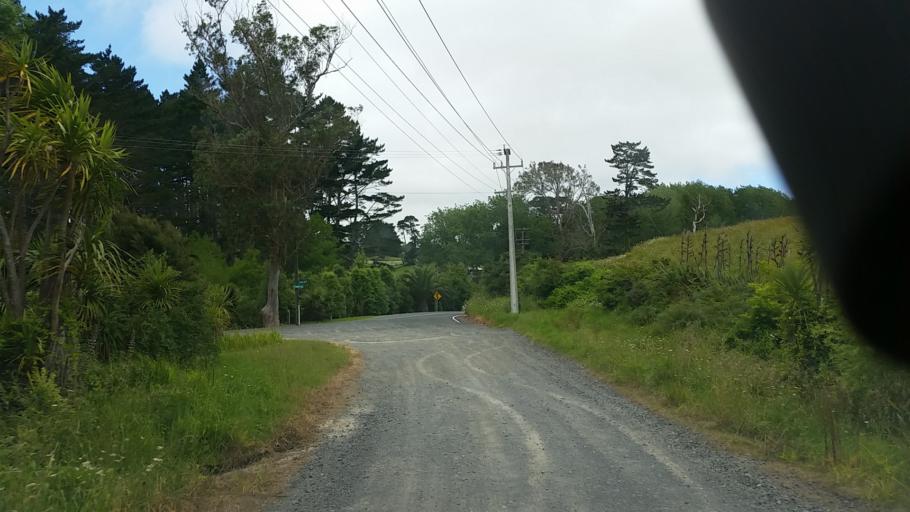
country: NZ
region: Auckland
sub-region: Auckland
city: Waitakere
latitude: -36.8783
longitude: 174.5821
